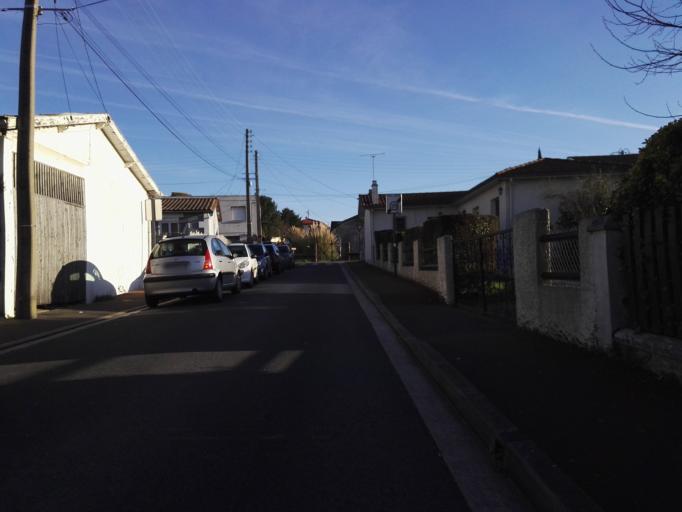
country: FR
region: Aquitaine
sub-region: Departement de la Gironde
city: Talence
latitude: 44.8196
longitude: -0.6136
